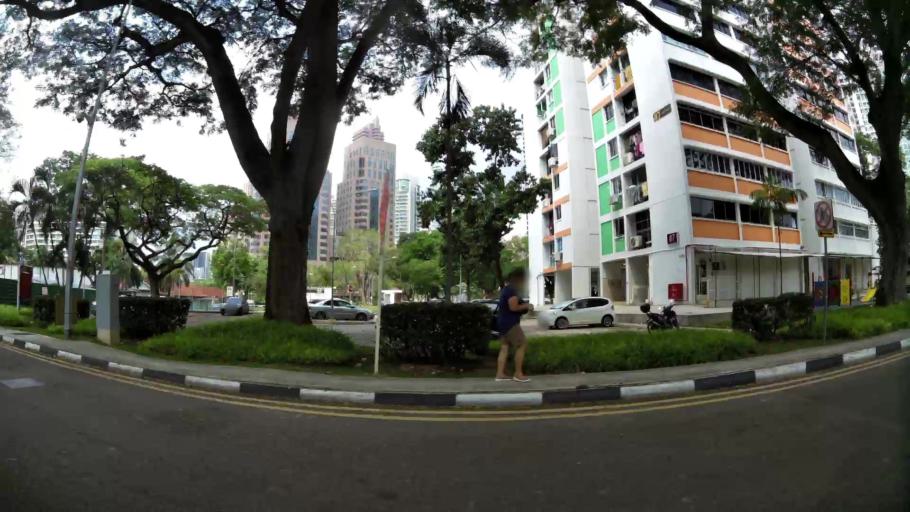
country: SG
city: Singapore
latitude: 1.2904
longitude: 103.8324
